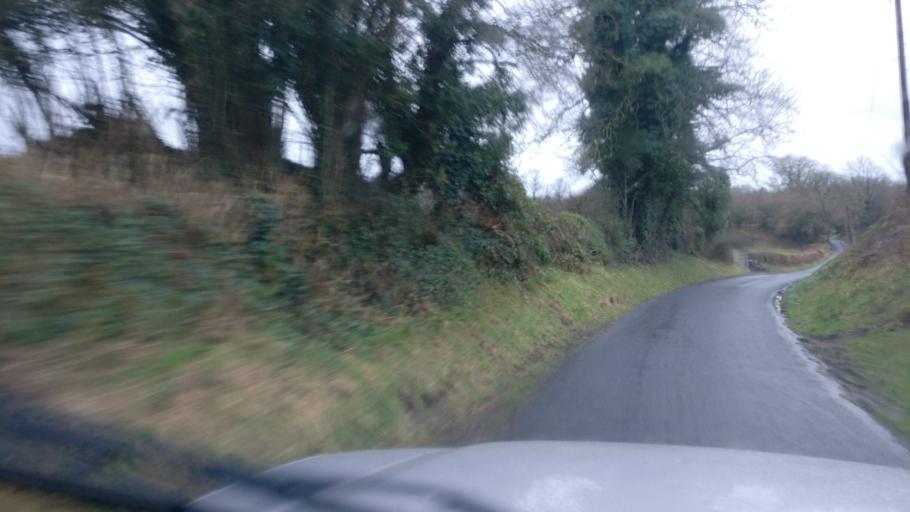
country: IE
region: Connaught
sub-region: County Galway
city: Ballinasloe
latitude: 53.2977
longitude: -8.2708
